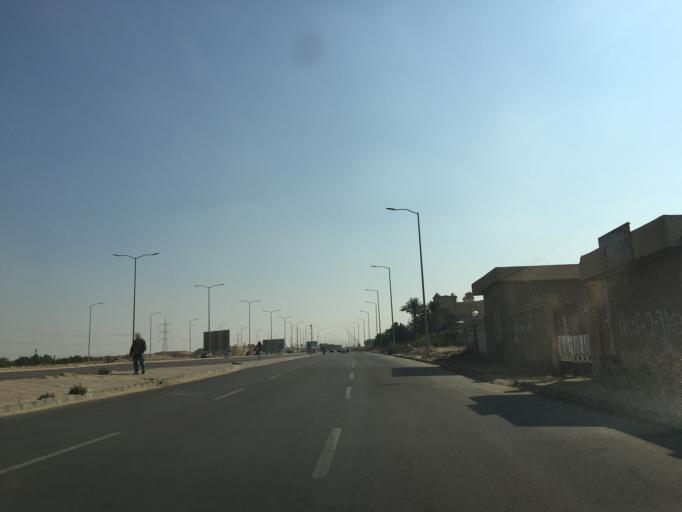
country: EG
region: Al Jizah
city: Awsim
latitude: 30.0052
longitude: 30.9845
